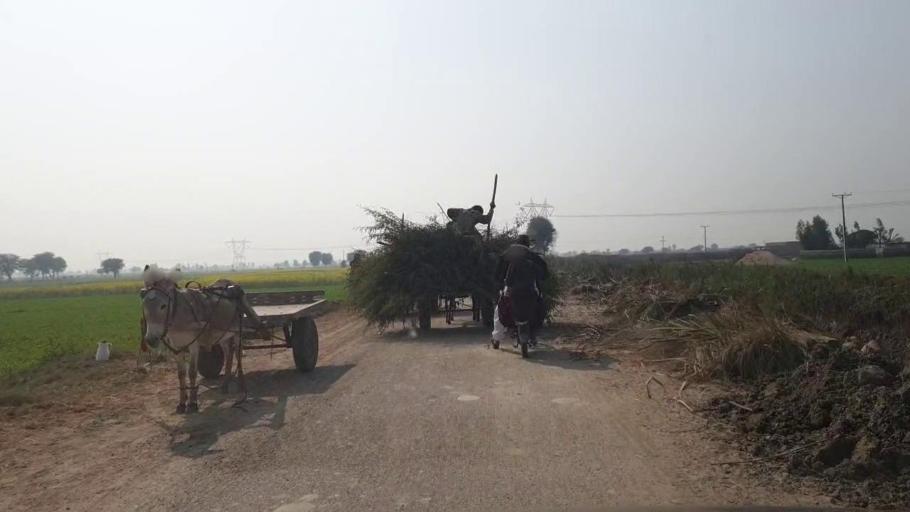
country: PK
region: Sindh
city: Hala
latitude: 25.9432
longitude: 68.4495
